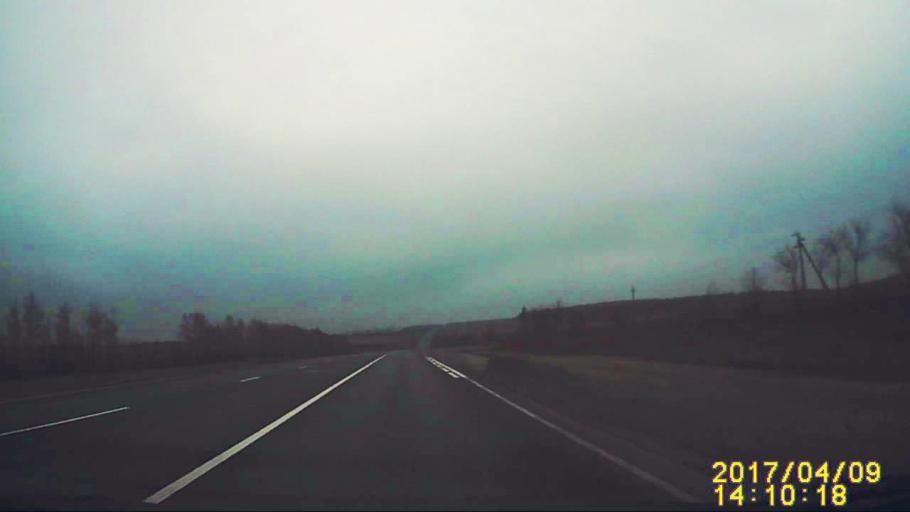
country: RU
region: Ulyanovsk
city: Krasnyy Gulyay
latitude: 54.0371
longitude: 48.2132
